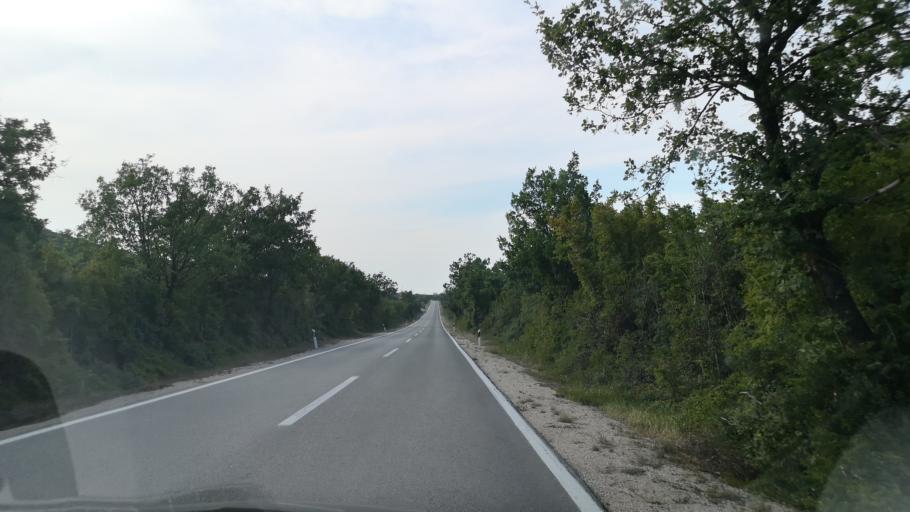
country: HR
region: Sibensko-Kniniska
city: Zaton
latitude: 43.8475
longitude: 15.7690
